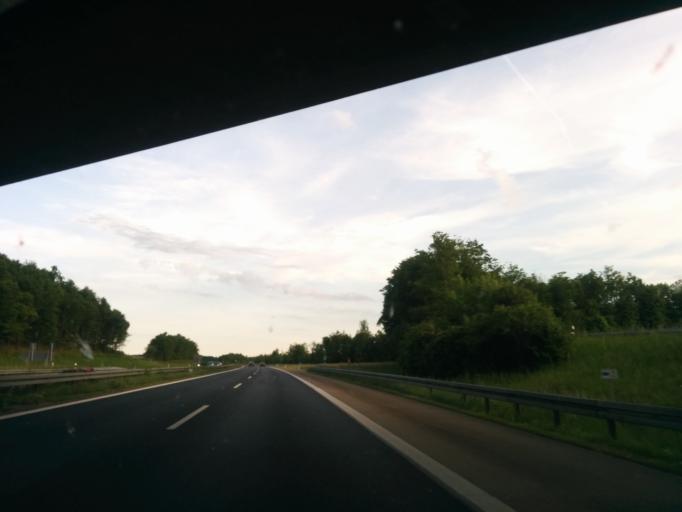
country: DE
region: Bavaria
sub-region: Regierungsbezirk Unterfranken
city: Riedenberg
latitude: 50.2959
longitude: 9.8492
